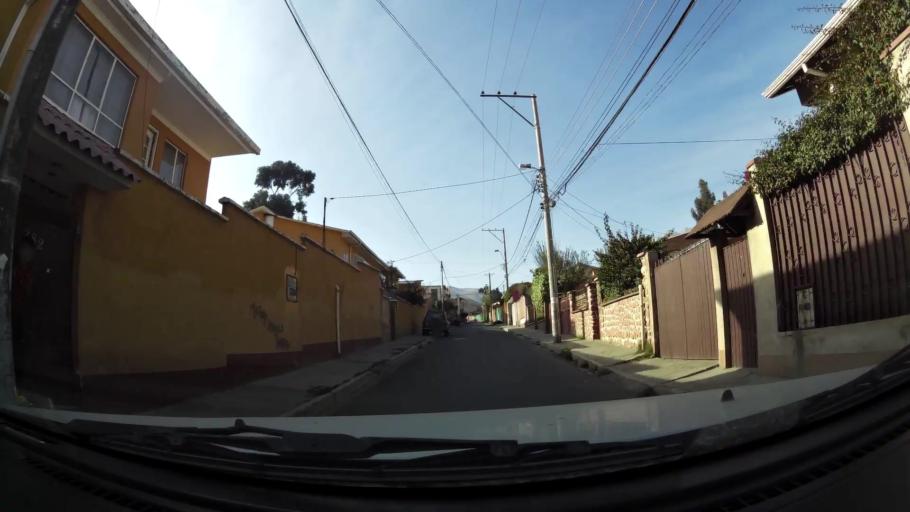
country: BO
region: La Paz
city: La Paz
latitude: -16.5248
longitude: -68.0901
